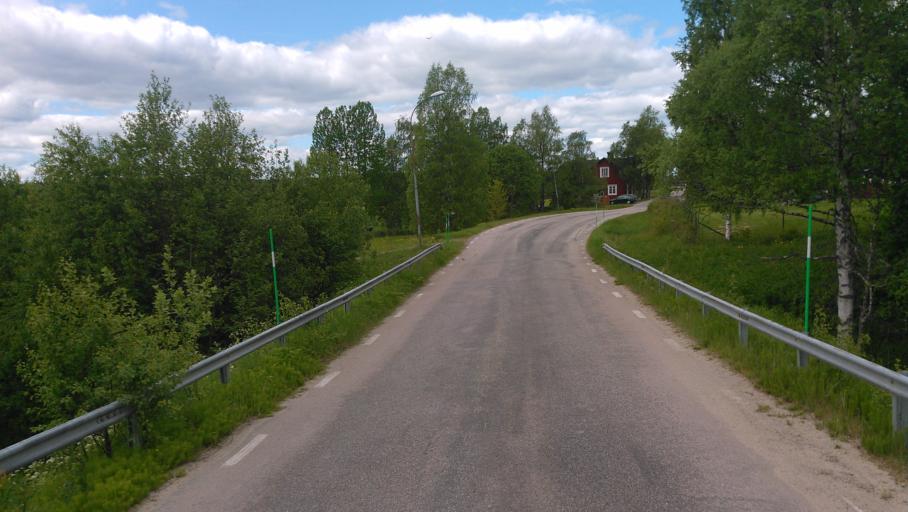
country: SE
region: Vaesterbotten
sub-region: Umea Kommun
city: Roback
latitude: 63.8635
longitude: 20.0856
